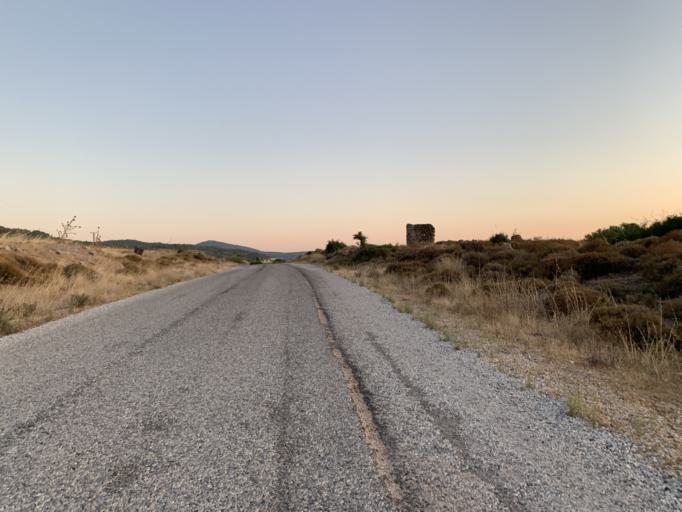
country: TR
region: Izmir
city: Uzunkuyu
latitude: 38.3283
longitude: 26.5840
